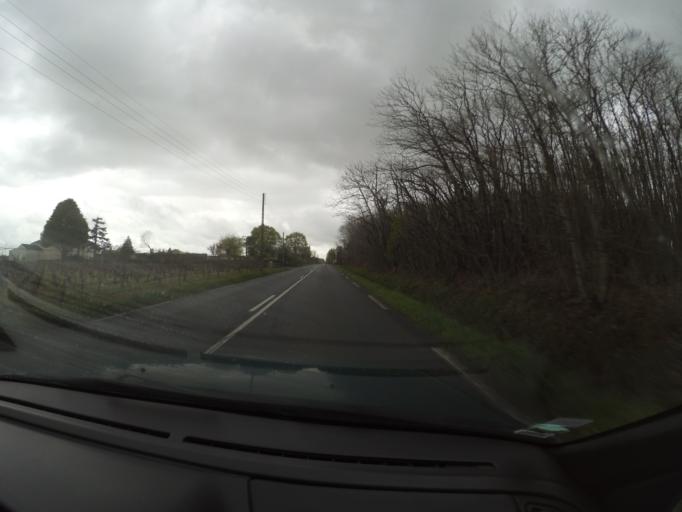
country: FR
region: Pays de la Loire
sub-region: Departement de la Loire-Atlantique
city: Vallet
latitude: 47.1855
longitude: -1.2556
